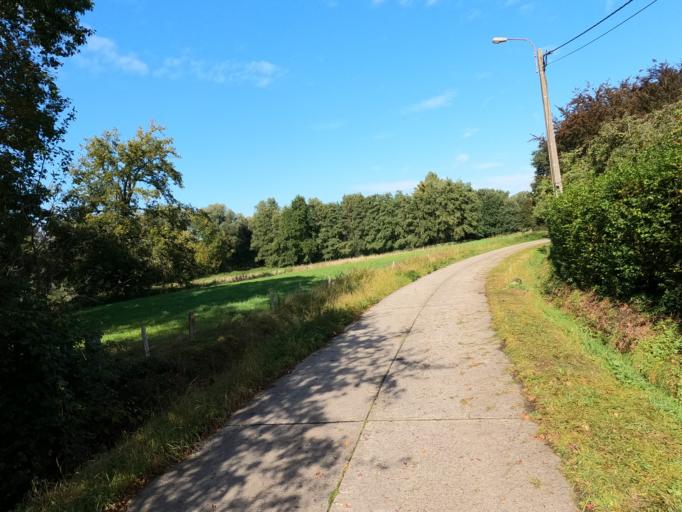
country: BE
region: Flanders
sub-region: Provincie Antwerpen
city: Lille
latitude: 51.2631
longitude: 4.8552
